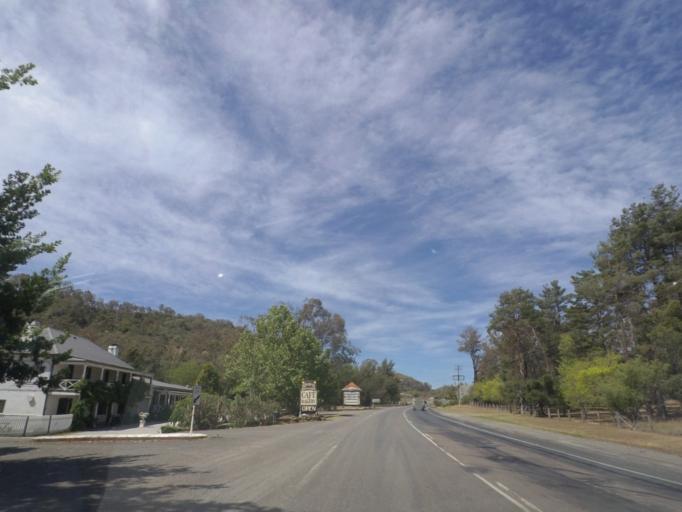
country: AU
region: New South Wales
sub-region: Wollondilly
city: Picton
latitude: -34.1637
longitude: 150.6352
